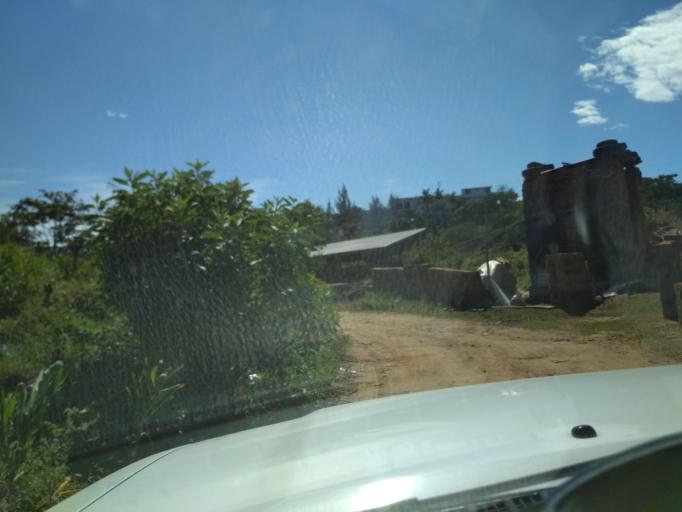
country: MX
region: Veracruz
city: El Castillo
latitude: 19.5459
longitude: -96.8528
